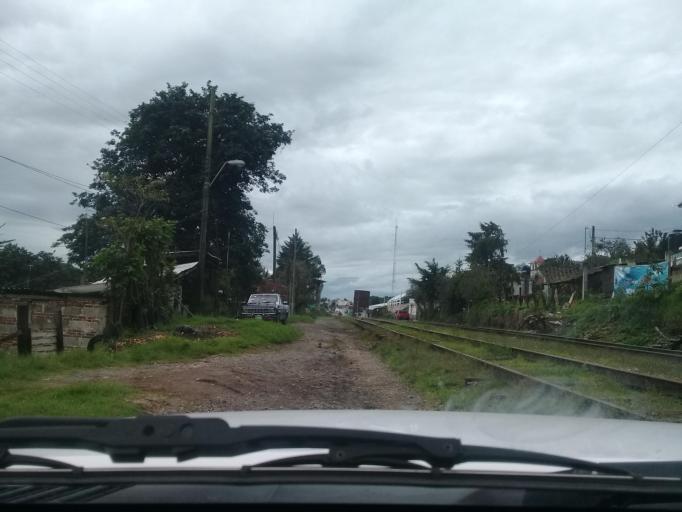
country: MX
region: Veracruz
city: Rafael Lucio
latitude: 19.5997
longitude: -96.9885
